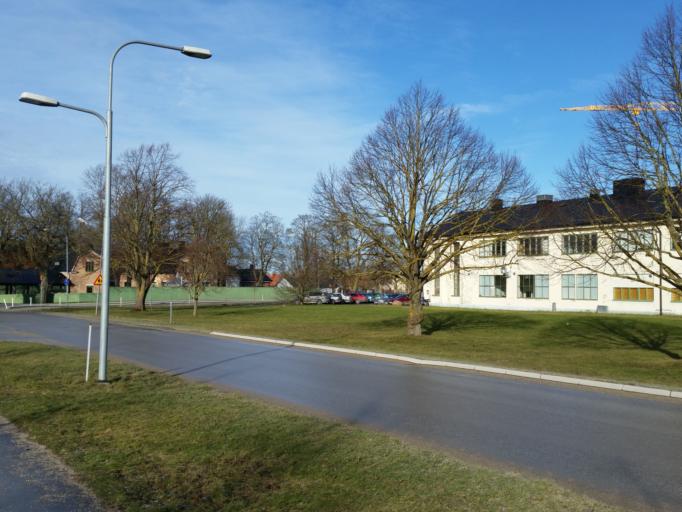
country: SE
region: Gotland
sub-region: Gotland
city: Visby
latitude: 57.6309
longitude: 18.3041
